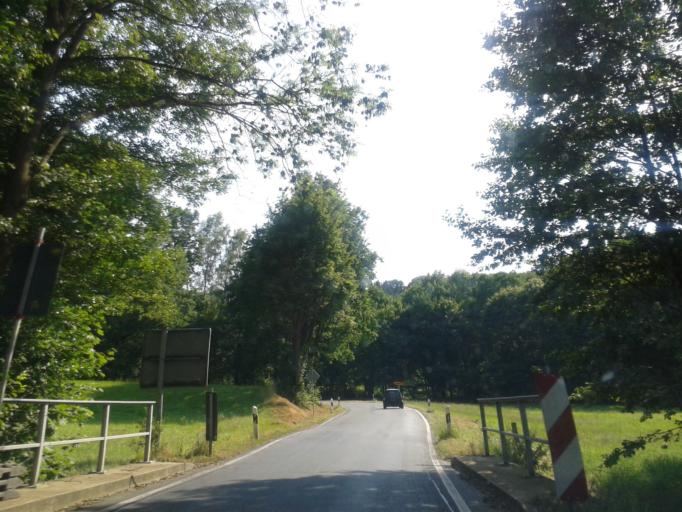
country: DE
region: Saxony
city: Reinsberg
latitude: 51.0189
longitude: 13.3438
